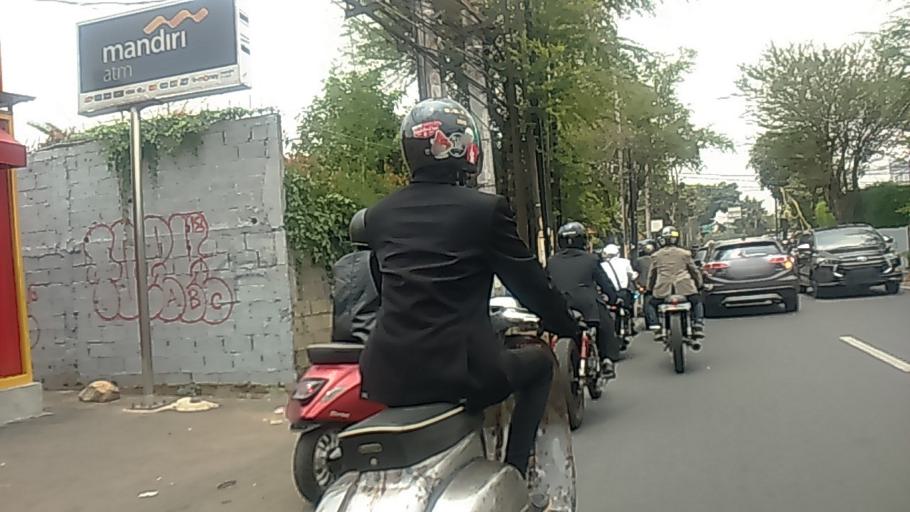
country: ID
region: West Java
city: Pamulang
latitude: -6.3002
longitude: 106.7760
